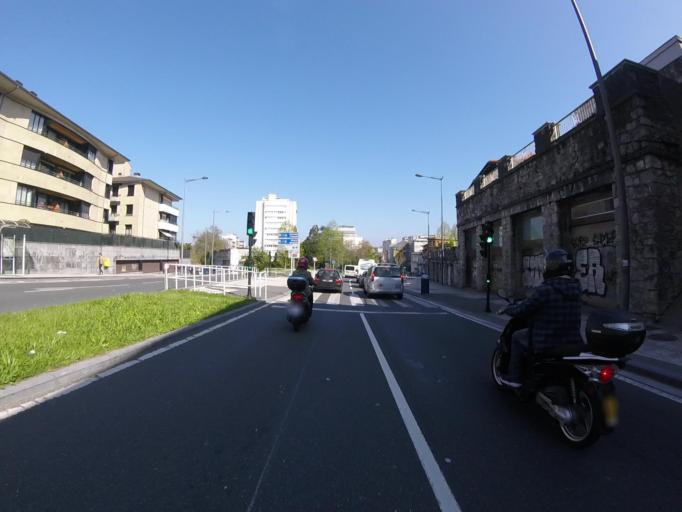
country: ES
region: Basque Country
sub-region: Provincia de Guipuzcoa
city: Pasaia
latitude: 43.3212
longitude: -1.9452
